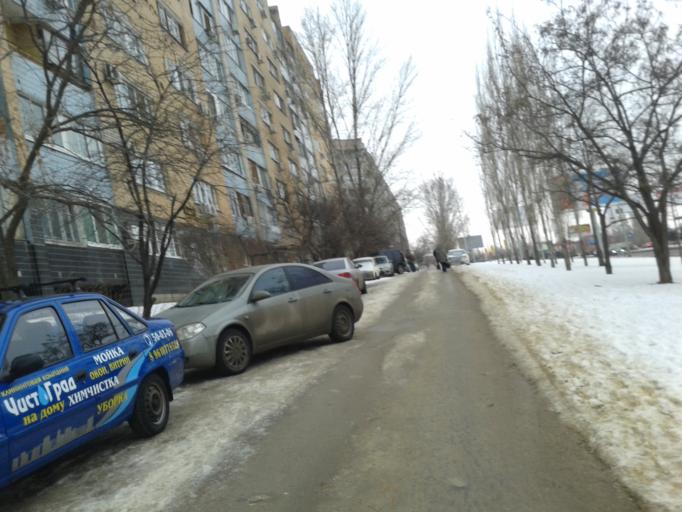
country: RU
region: Volgograd
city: Volgograd
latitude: 48.7261
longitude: 44.5239
